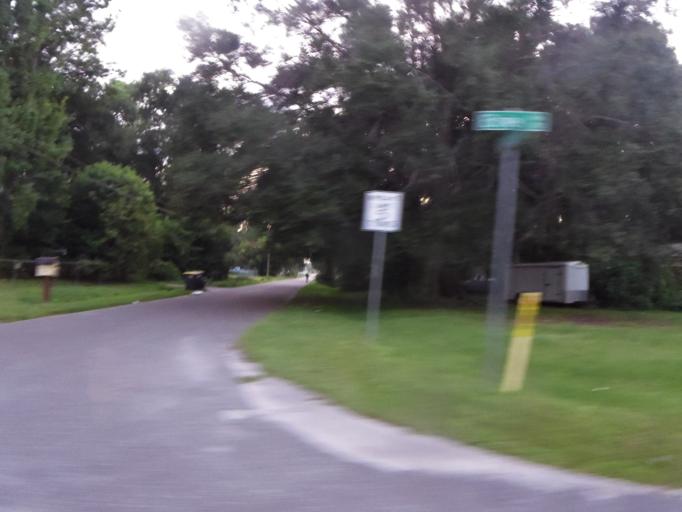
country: US
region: Florida
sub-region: Duval County
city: Jacksonville
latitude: 30.3304
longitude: -81.7268
